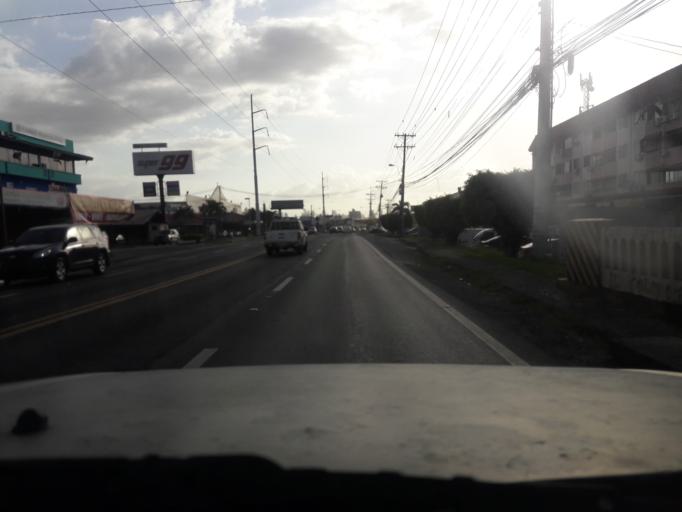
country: PA
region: Panama
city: San Miguelito
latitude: 9.0313
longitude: -79.4755
